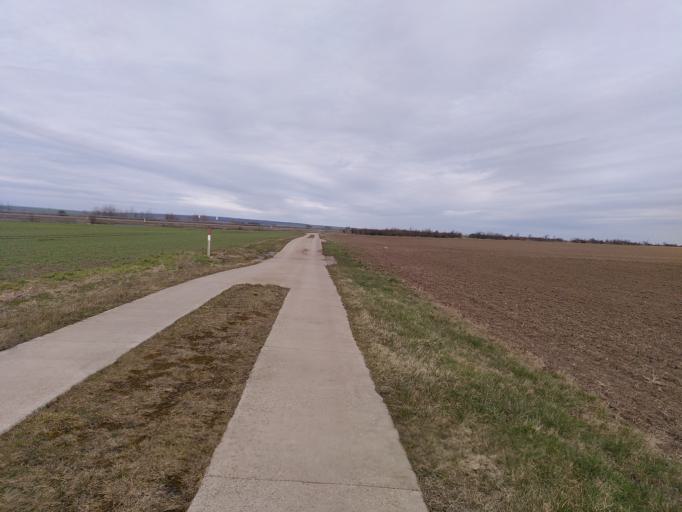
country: DE
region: Saxony-Anhalt
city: Gatersleben
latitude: 51.8021
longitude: 11.2621
